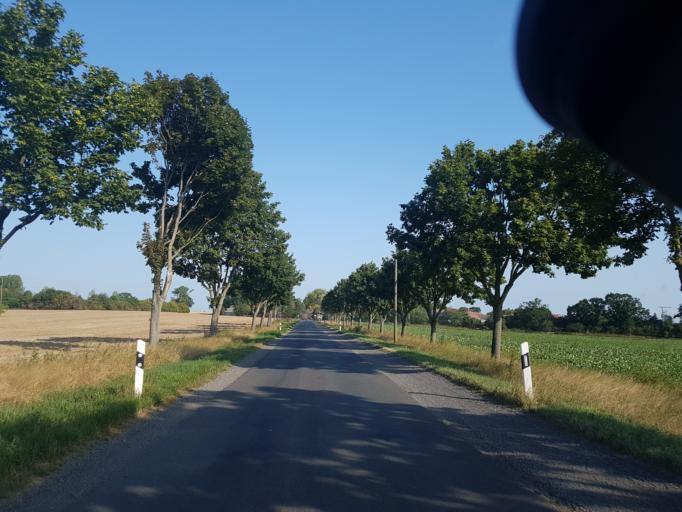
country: DE
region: Brandenburg
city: Niemegk
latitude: 52.0225
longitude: 12.6831
